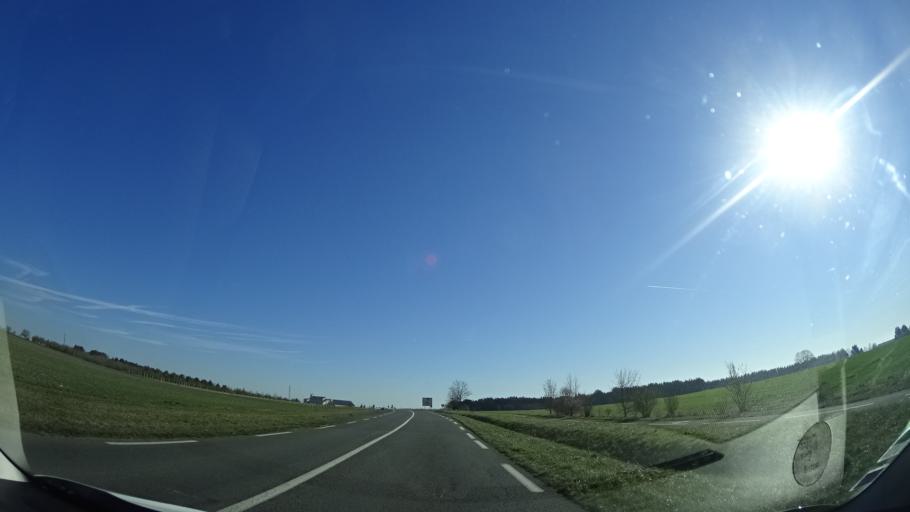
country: FR
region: Poitou-Charentes
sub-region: Departement de la Vienne
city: Jaunay-Clan
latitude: 46.6839
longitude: 0.3516
